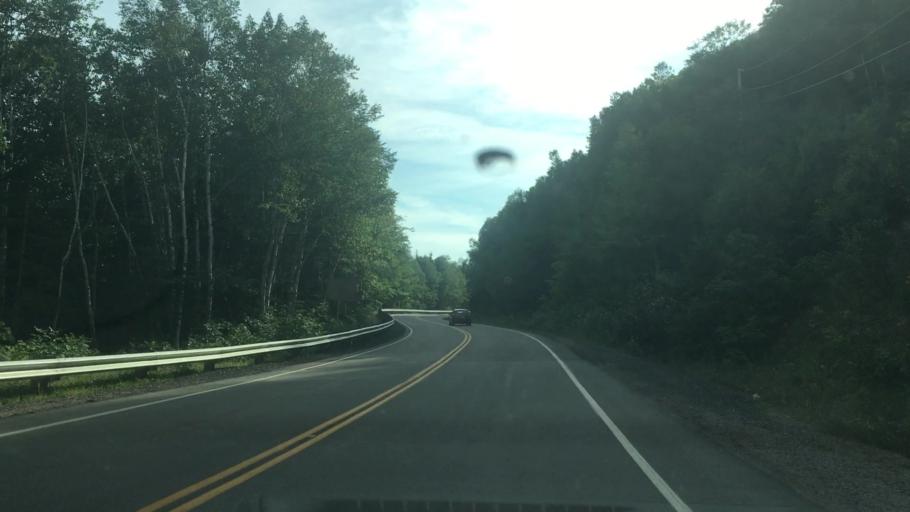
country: CA
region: Nova Scotia
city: Sydney Mines
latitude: 46.8275
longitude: -60.6209
